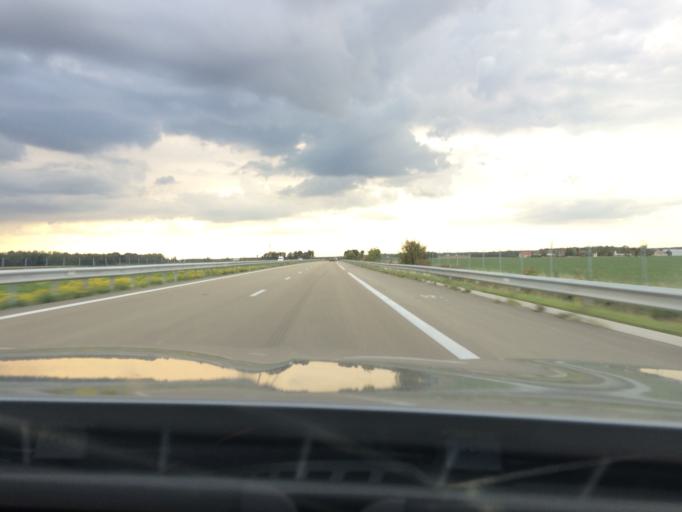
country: FR
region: Centre
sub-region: Departement du Loiret
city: Dordives
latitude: 48.1979
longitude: 2.8062
